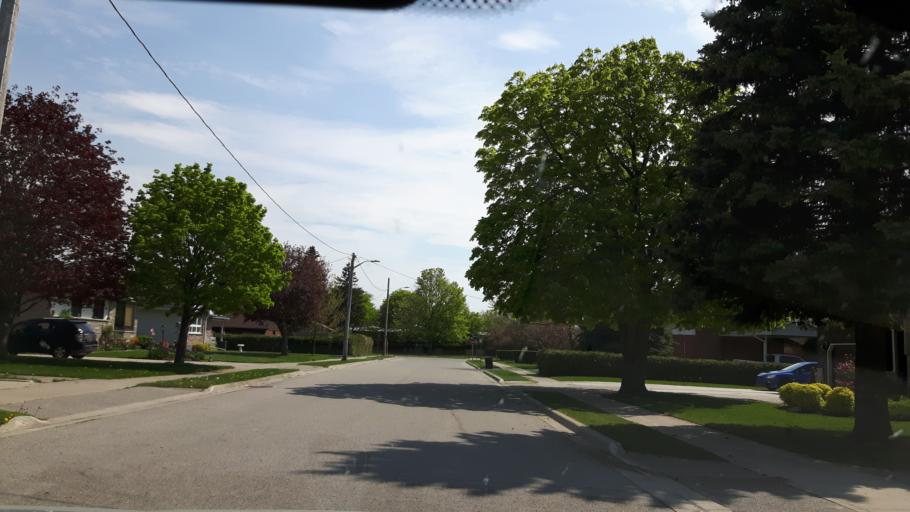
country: CA
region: Ontario
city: Goderich
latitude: 43.7363
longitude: -81.7179
